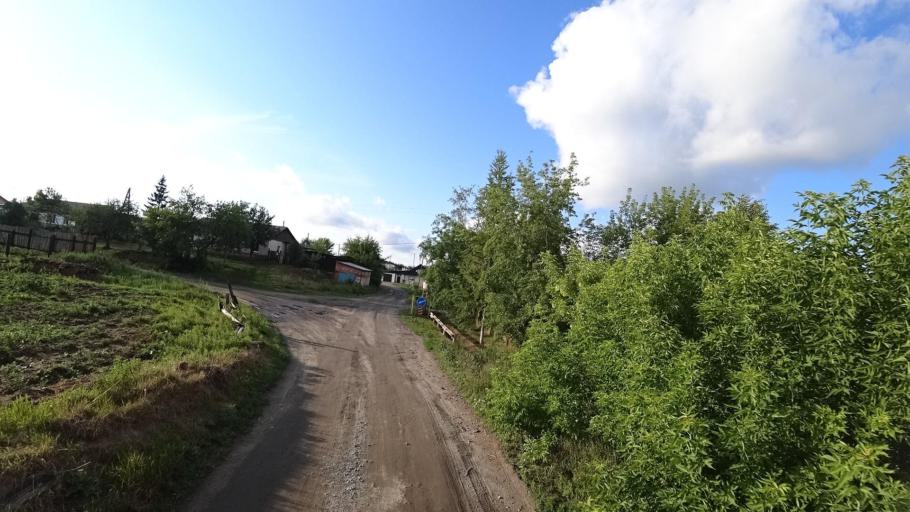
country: RU
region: Sverdlovsk
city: Kamyshlov
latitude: 56.8496
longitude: 62.6710
